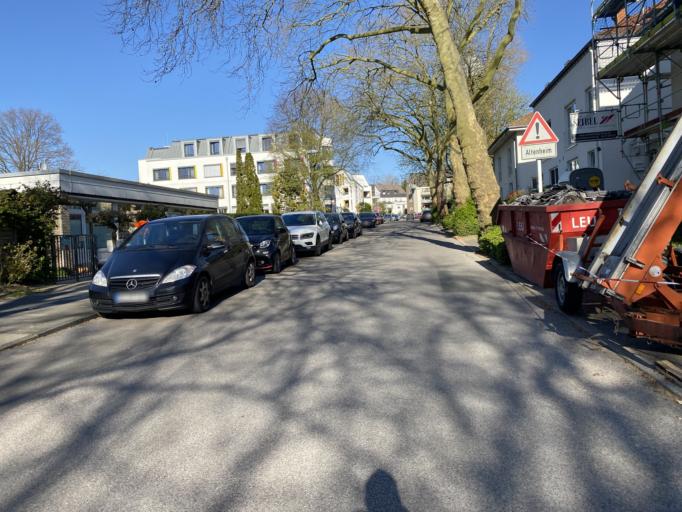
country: DE
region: North Rhine-Westphalia
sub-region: Regierungsbezirk Dusseldorf
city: Velbert
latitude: 51.3999
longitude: 7.0615
